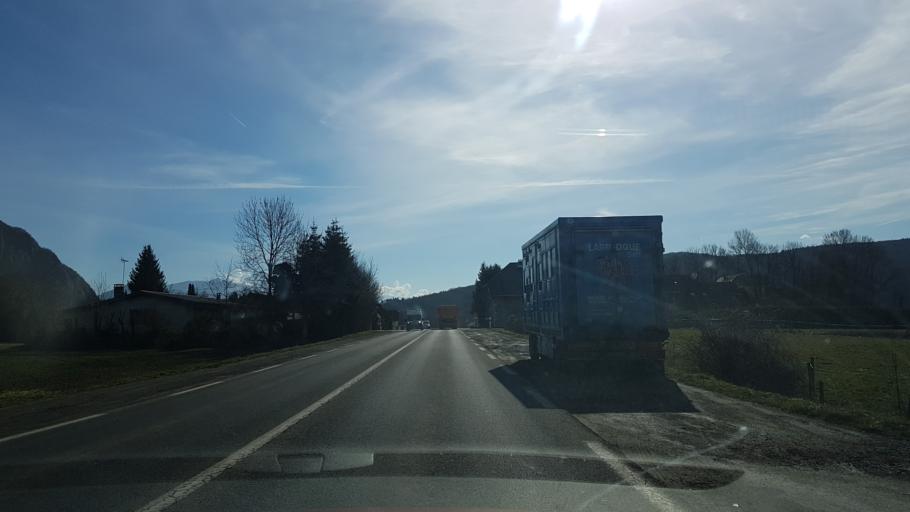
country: FR
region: Rhone-Alpes
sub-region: Departement de la Haute-Savoie
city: La Balme-de-Sillingy
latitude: 45.9510
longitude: 6.0436
